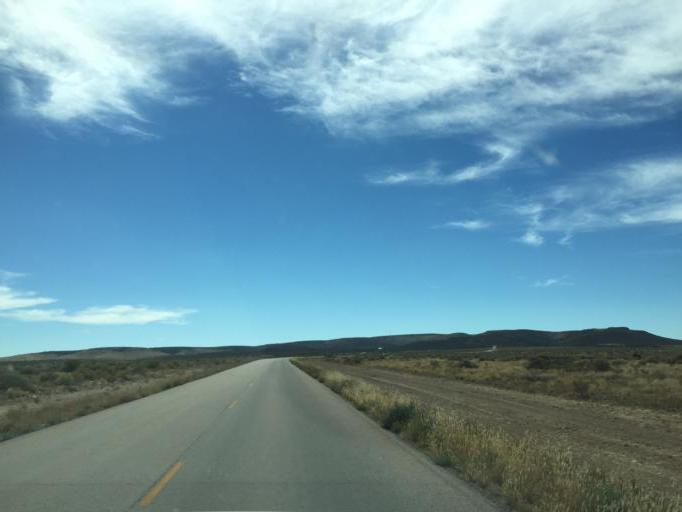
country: US
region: Arizona
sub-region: Mohave County
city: Meadview
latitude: 35.9506
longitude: -113.8493
